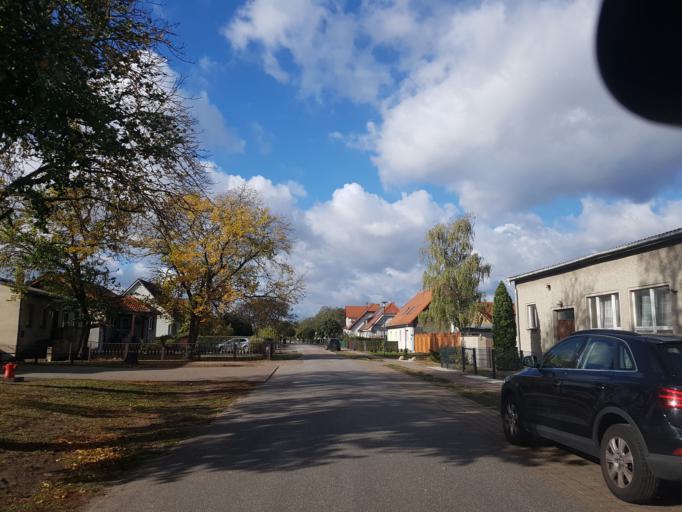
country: DE
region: Brandenburg
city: Nauen
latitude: 52.6633
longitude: 12.9044
